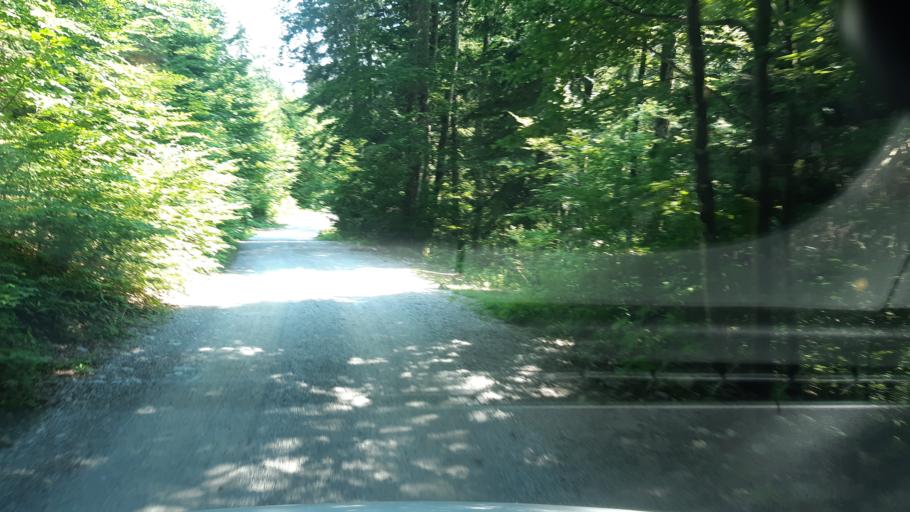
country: SI
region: Trzic
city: Bistrica pri Trzicu
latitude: 46.3763
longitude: 14.2761
